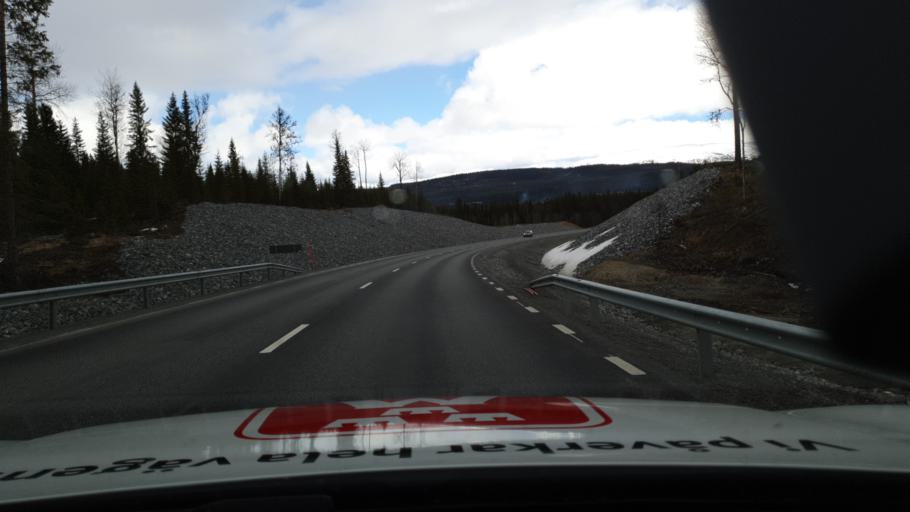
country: SE
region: Jaemtland
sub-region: Are Kommun
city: Are
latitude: 63.3954
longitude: 12.7807
